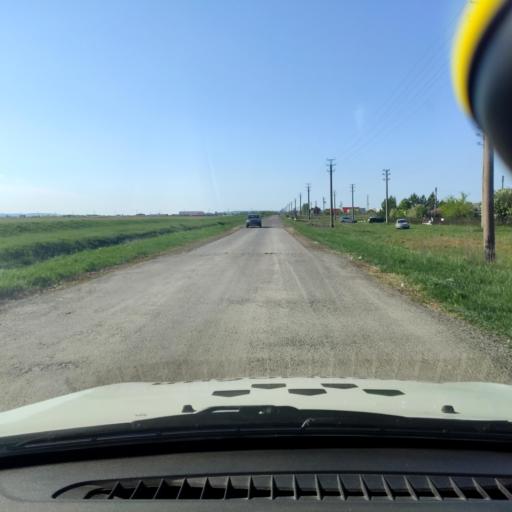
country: RU
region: Samara
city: Podstepki
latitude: 53.5319
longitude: 49.1982
